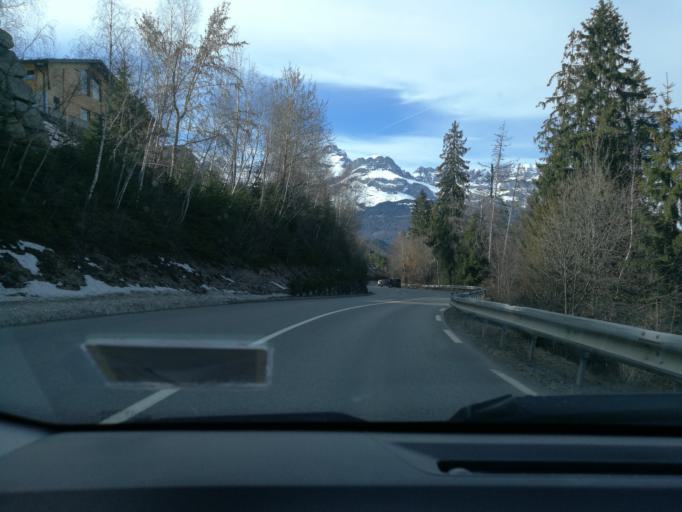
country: FR
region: Rhone-Alpes
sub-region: Departement de la Haute-Savoie
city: Domancy
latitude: 45.9003
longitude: 6.6500
